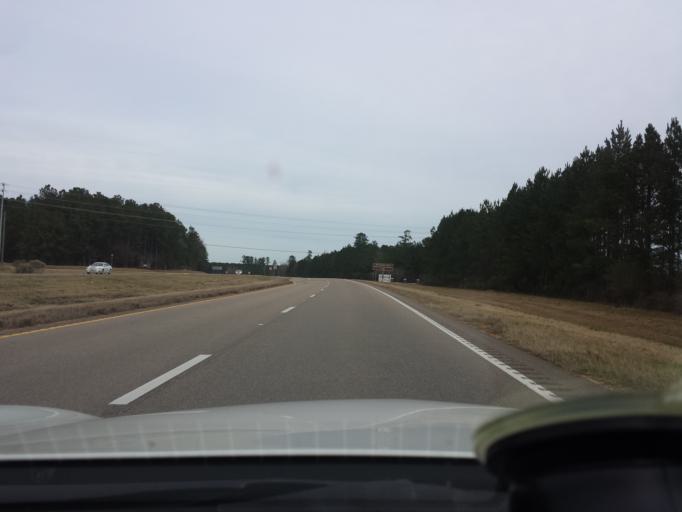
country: US
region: Mississippi
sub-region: Oktibbeha County
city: Starkville
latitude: 33.4015
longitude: -88.8566
